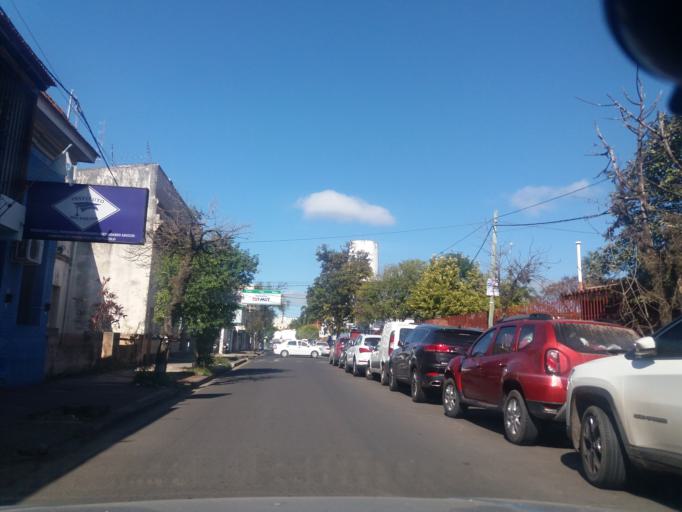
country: AR
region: Corrientes
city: Corrientes
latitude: -27.4741
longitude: -58.8352
